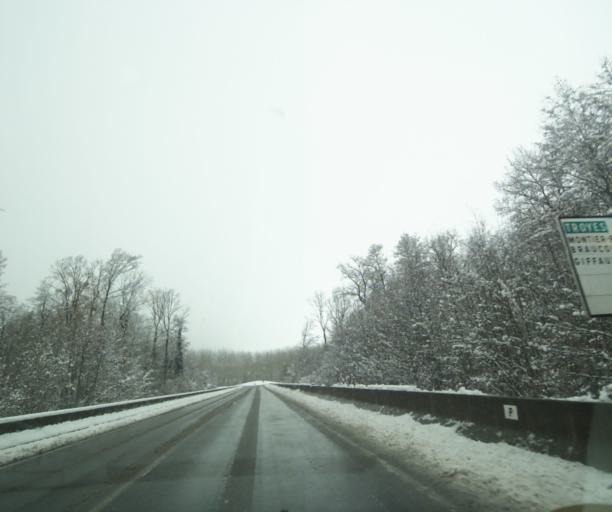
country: FR
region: Champagne-Ardenne
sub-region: Departement de la Haute-Marne
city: Villiers-en-Lieu
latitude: 48.5794
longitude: 4.8587
